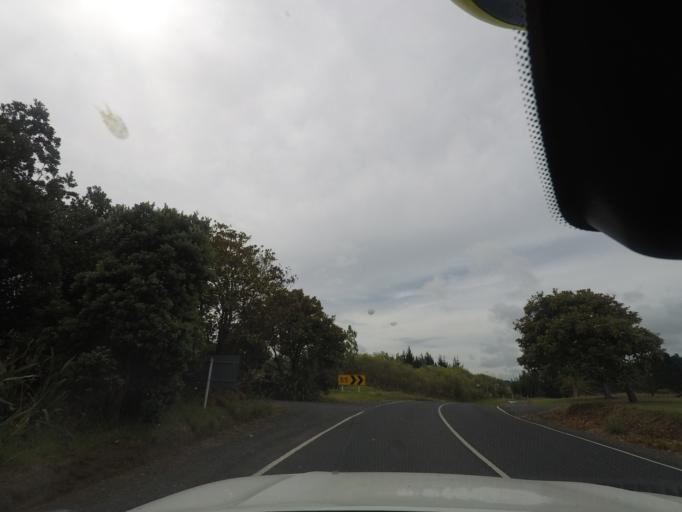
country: NZ
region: Auckland
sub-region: Auckland
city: Parakai
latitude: -36.5132
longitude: 174.2478
